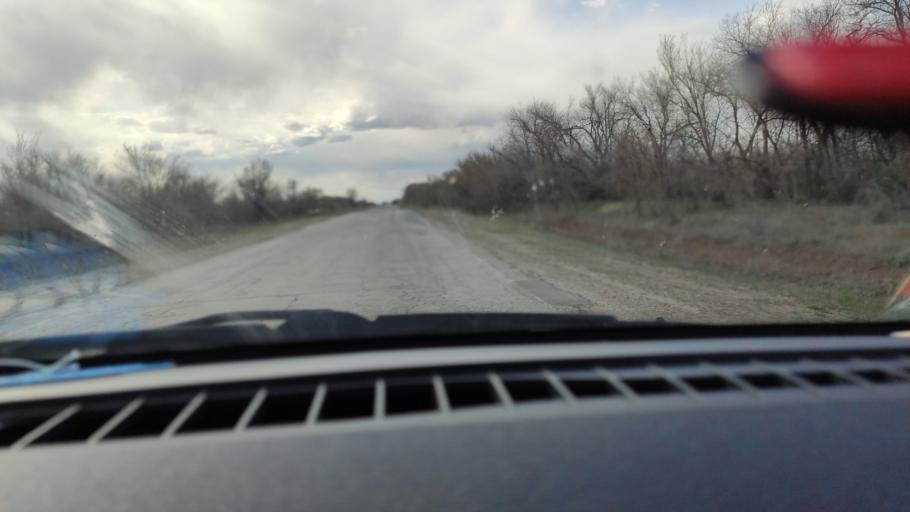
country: RU
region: Saratov
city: Rovnoye
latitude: 51.0416
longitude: 46.0664
